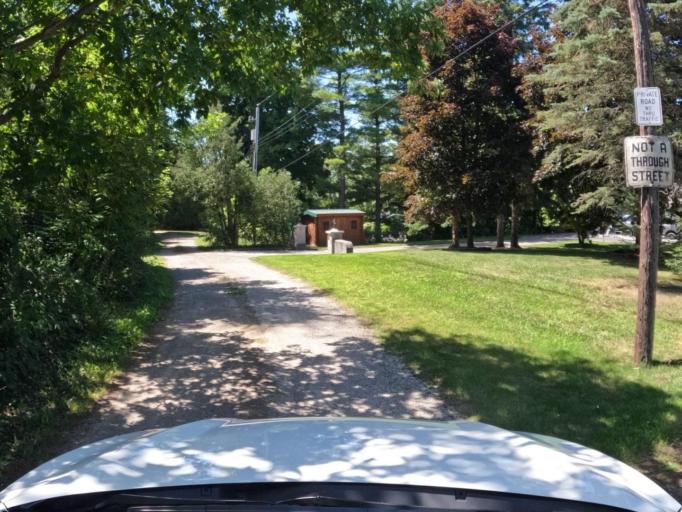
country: CA
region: Ontario
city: Cambridge
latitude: 43.4132
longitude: -80.2543
